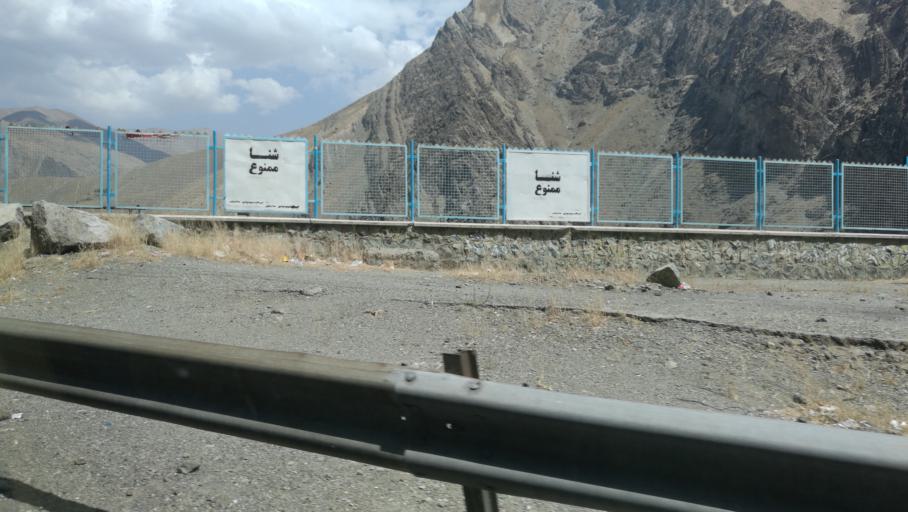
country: IR
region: Alborz
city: Karaj
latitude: 35.9604
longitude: 51.0902
